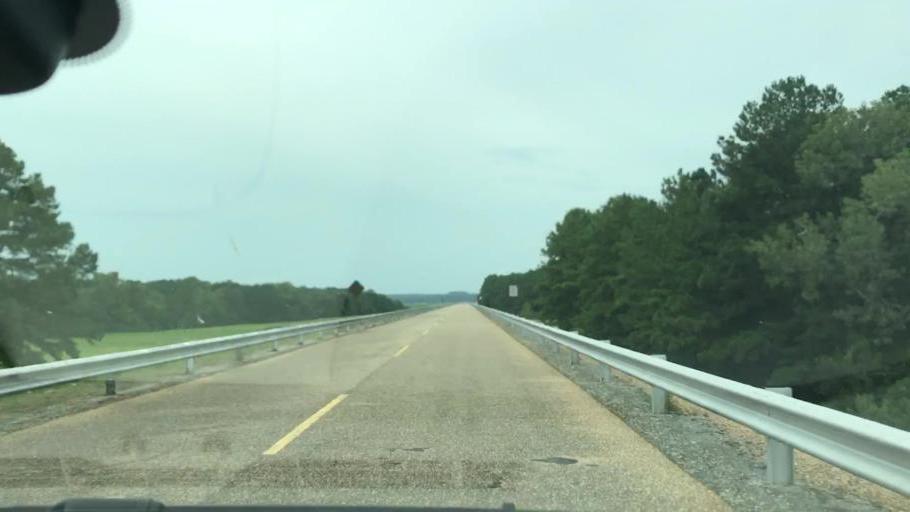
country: US
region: Georgia
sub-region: Clay County
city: Fort Gaines
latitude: 31.6314
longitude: -85.0467
